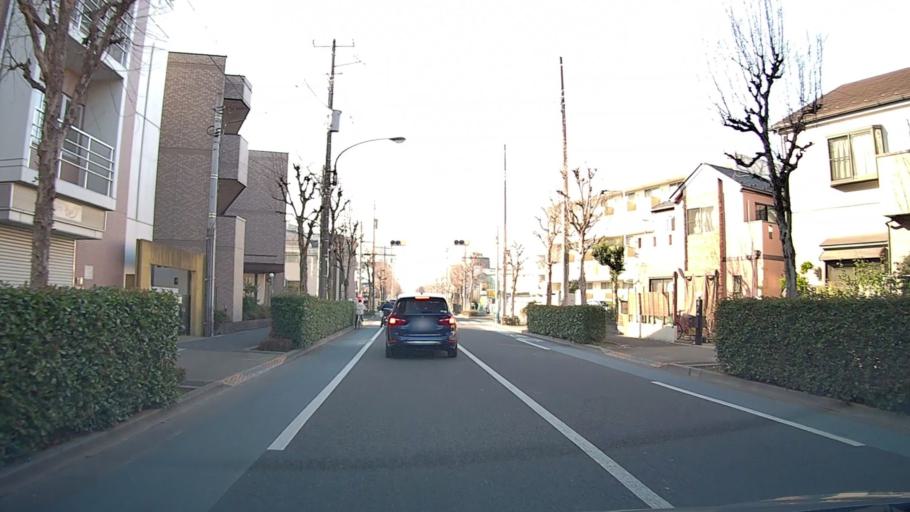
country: JP
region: Saitama
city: Wako
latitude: 35.7489
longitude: 139.6478
